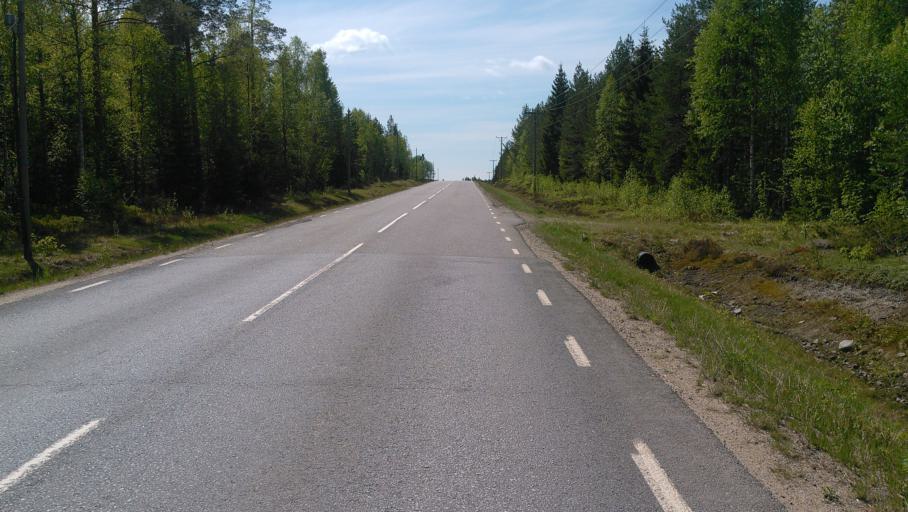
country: SE
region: Vaesterbotten
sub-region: Umea Kommun
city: Roback
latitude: 63.8599
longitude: 20.0056
